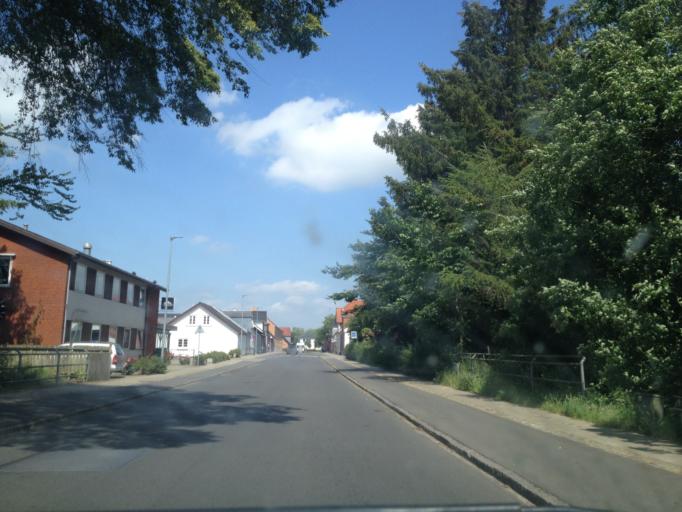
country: DK
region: South Denmark
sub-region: Kolding Kommune
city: Vamdrup
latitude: 55.4240
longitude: 9.2795
